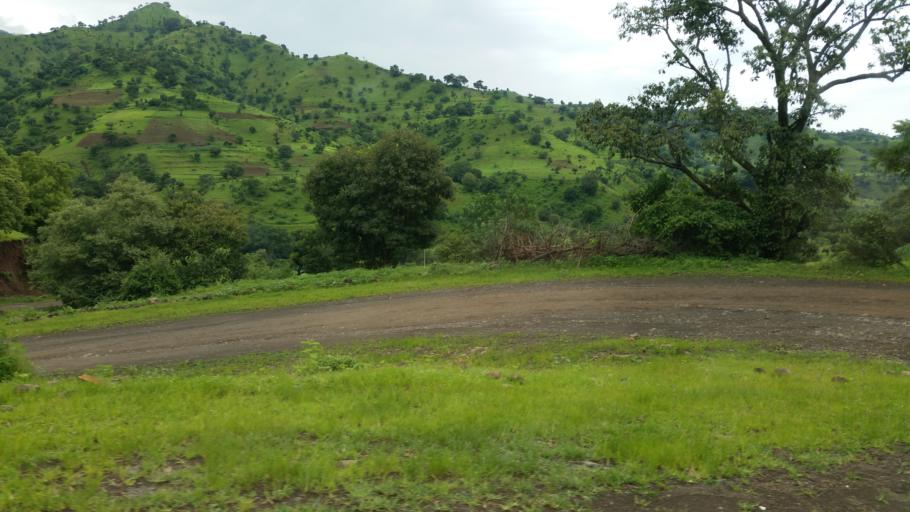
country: ET
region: Amhara
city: Debark'
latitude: 13.2838
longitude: 37.8623
